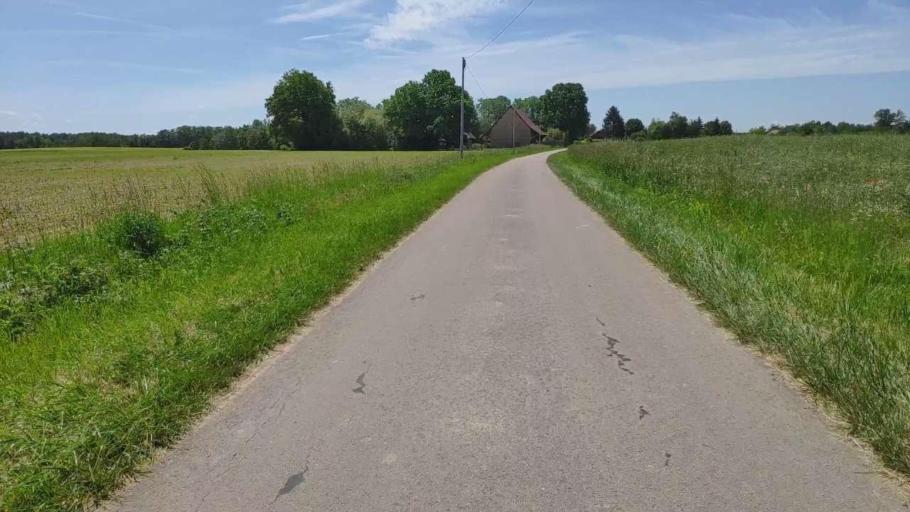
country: FR
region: Franche-Comte
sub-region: Departement du Jura
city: Bletterans
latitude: 46.8014
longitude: 5.3993
